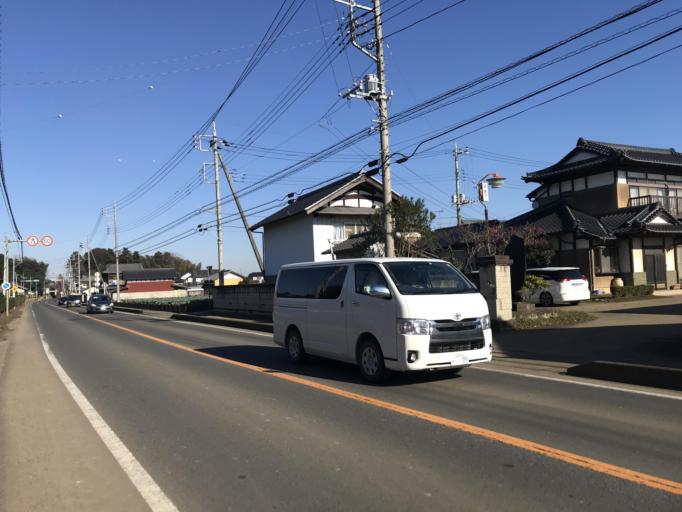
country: JP
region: Tochigi
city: Oyama
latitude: 36.2227
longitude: 139.8240
